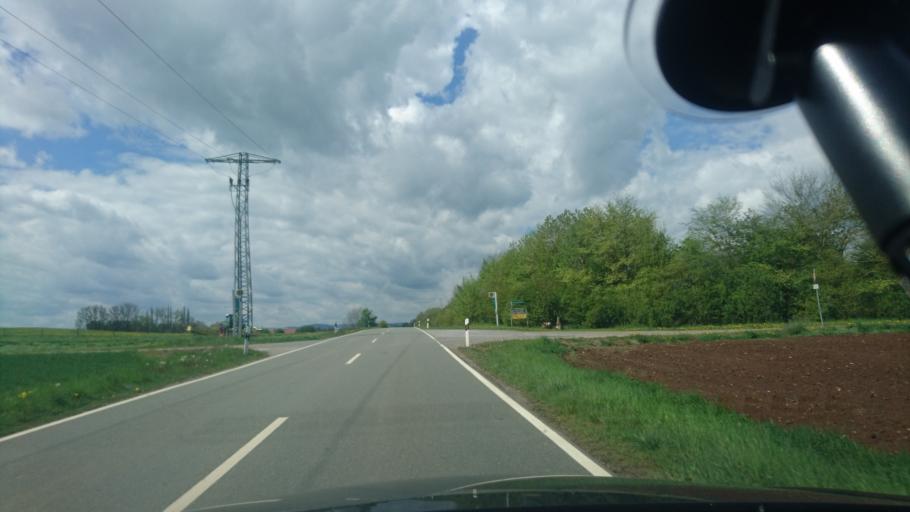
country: DE
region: North Rhine-Westphalia
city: Marsberg
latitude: 51.3706
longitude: 8.8358
